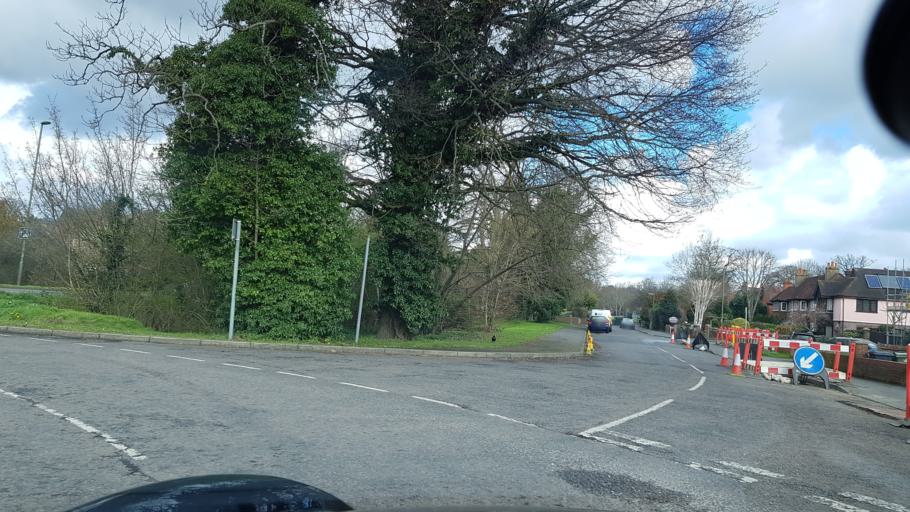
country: GB
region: England
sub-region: Surrey
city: Guildford
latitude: 51.2596
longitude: -0.5731
